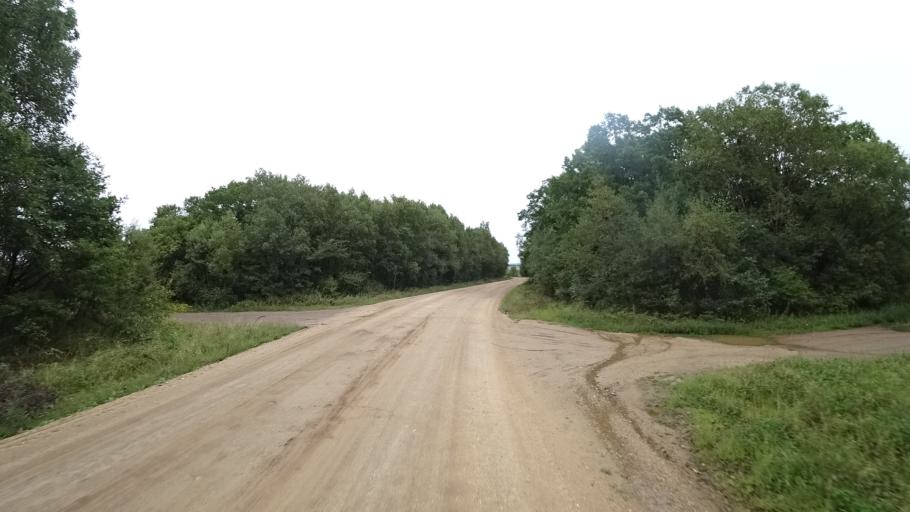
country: RU
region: Primorskiy
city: Ivanovka
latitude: 44.0585
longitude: 132.5616
